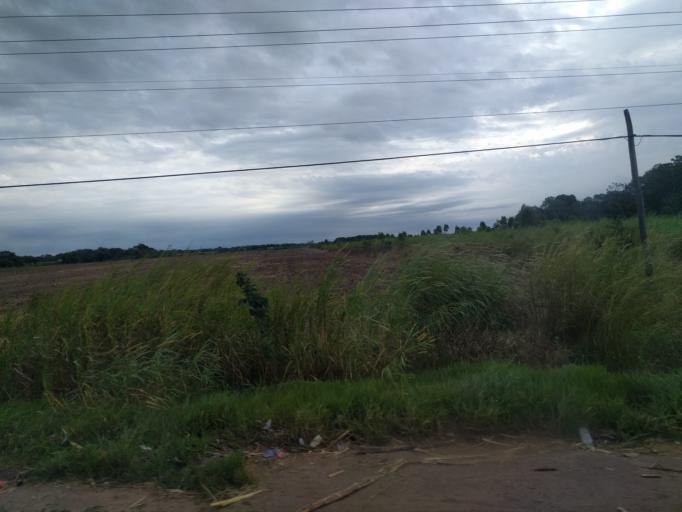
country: BO
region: Santa Cruz
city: Warnes
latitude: -17.4825
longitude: -63.1811
